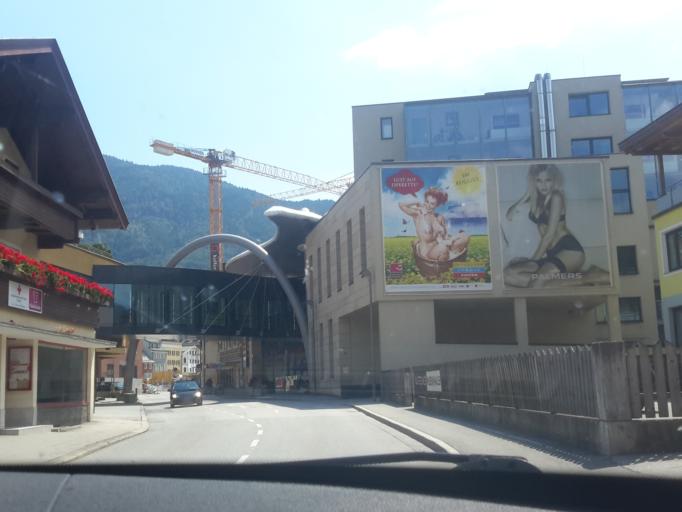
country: AT
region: Tyrol
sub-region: Politischer Bezirk Kufstein
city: Kufstein
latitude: 47.5853
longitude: 12.1698
